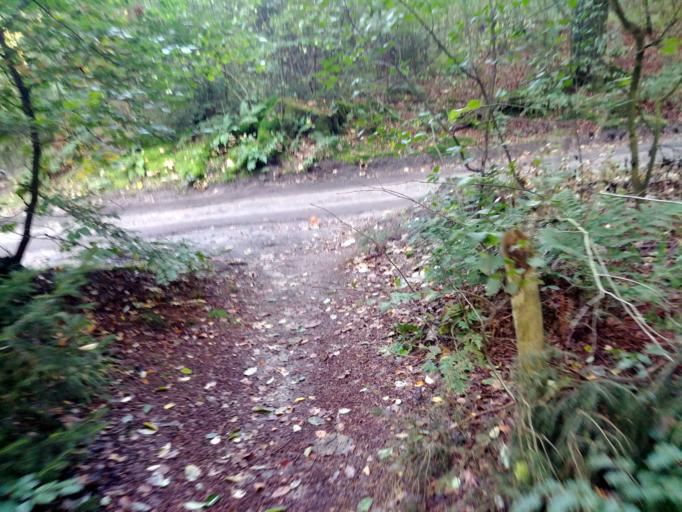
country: NL
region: Gelderland
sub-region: Gemeente Renkum
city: Heelsum
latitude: 52.0085
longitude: 5.7394
